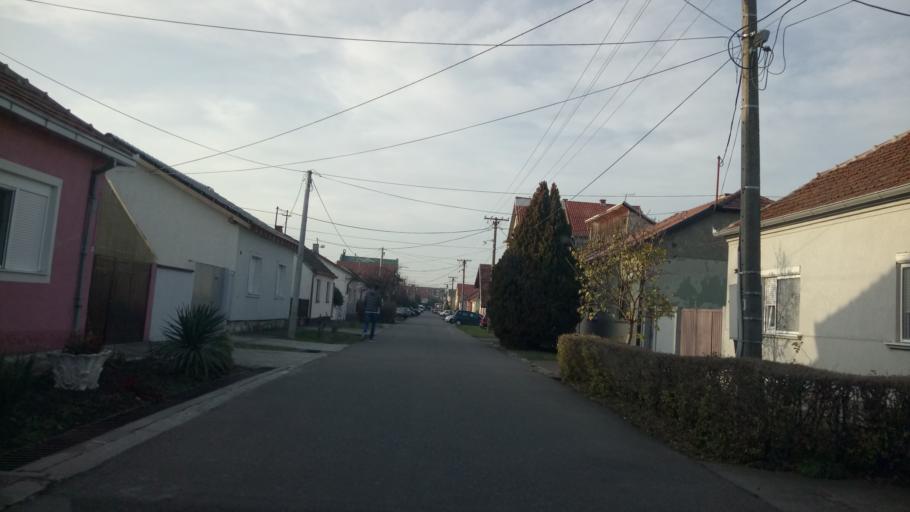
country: RS
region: Autonomna Pokrajina Vojvodina
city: Nova Pazova
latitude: 44.9371
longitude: 20.2274
